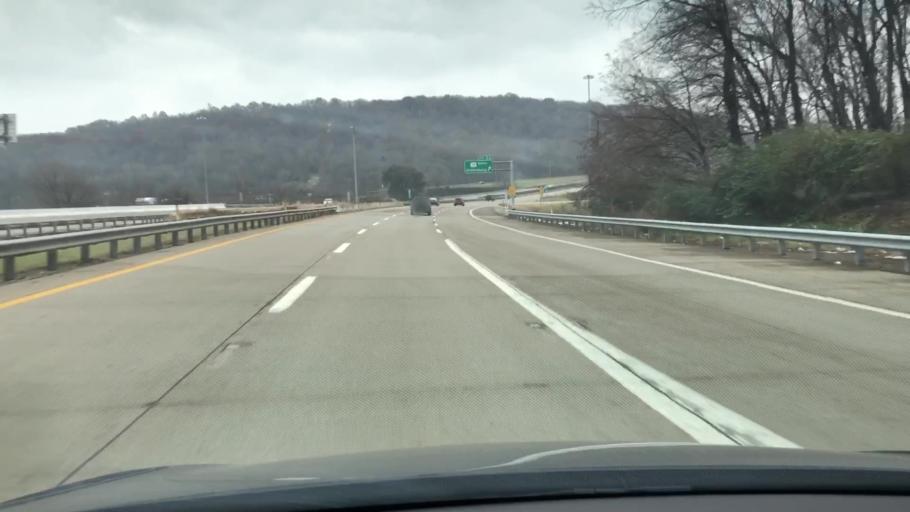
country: US
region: Pennsylvania
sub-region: Westmoreland County
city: New Stanton
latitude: 40.2264
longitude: -79.5946
